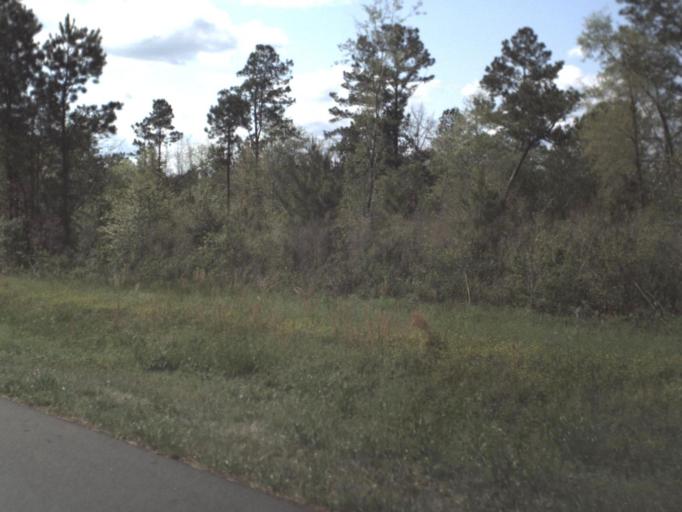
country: US
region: Alabama
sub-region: Covington County
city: Florala
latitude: 30.9668
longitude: -86.4099
